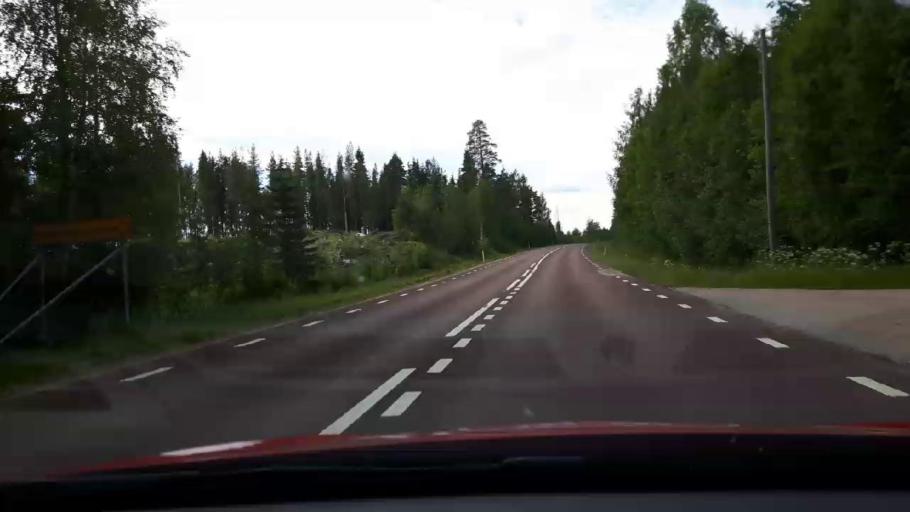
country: SE
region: Jaemtland
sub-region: Harjedalens Kommun
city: Sveg
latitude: 62.0692
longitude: 14.9342
